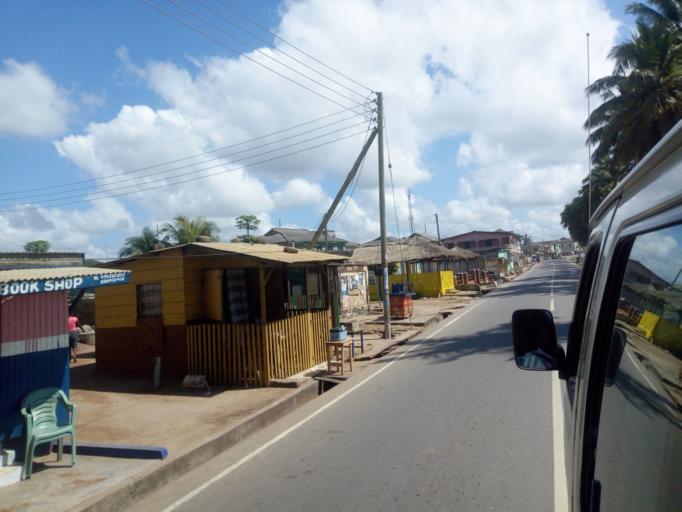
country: GH
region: Central
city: Elmina
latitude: 5.0893
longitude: -1.3474
